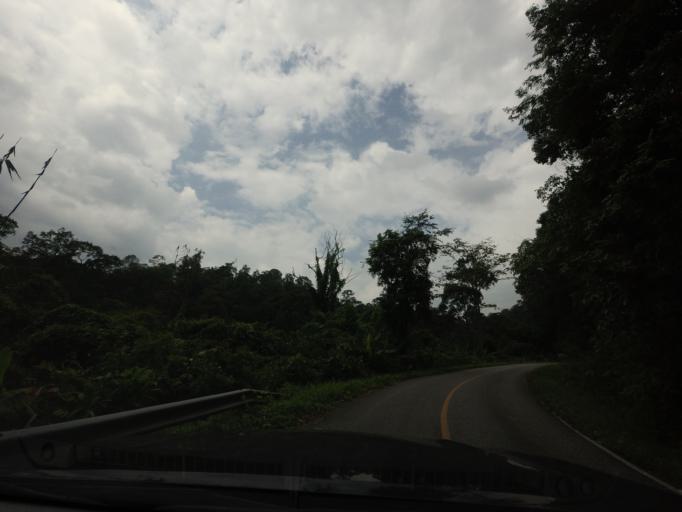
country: TH
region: Loei
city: Na Haeo
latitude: 17.7093
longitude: 100.9467
